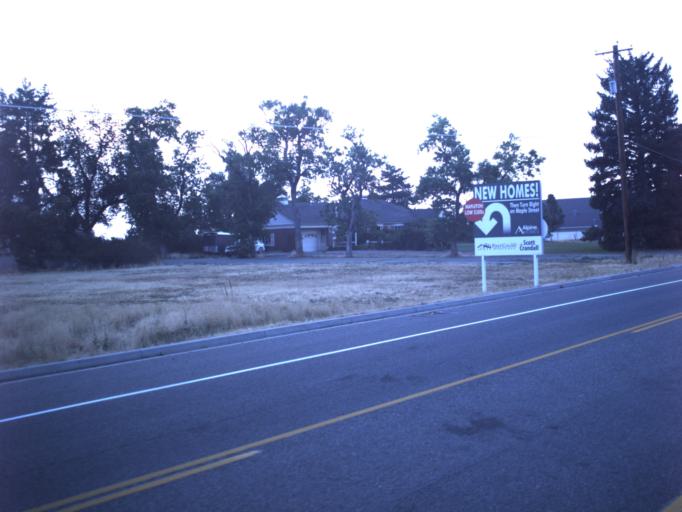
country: US
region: Utah
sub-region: Utah County
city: Mapleton
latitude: 40.1328
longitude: -111.5979
